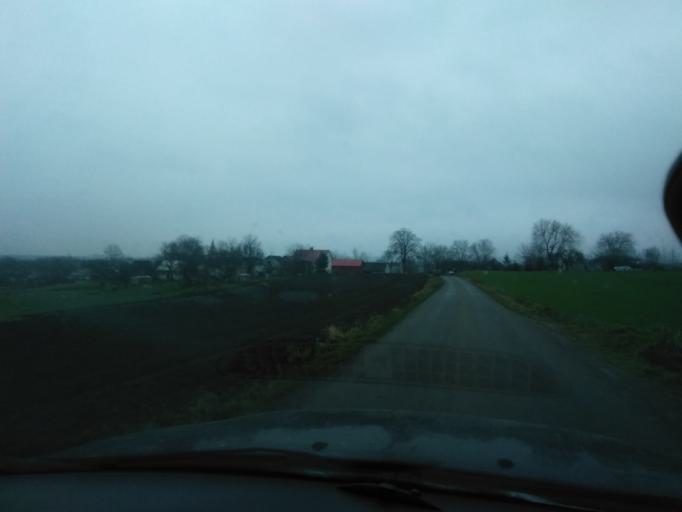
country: PL
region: Subcarpathian Voivodeship
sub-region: Powiat jaroslawski
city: Rokietnica
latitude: 49.9189
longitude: 22.6164
